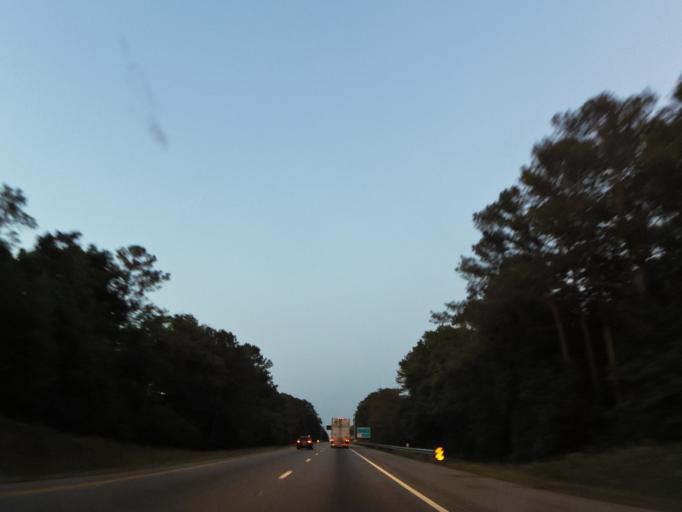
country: US
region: Tennessee
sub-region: Bradley County
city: Cleveland
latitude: 35.1437
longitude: -84.9774
